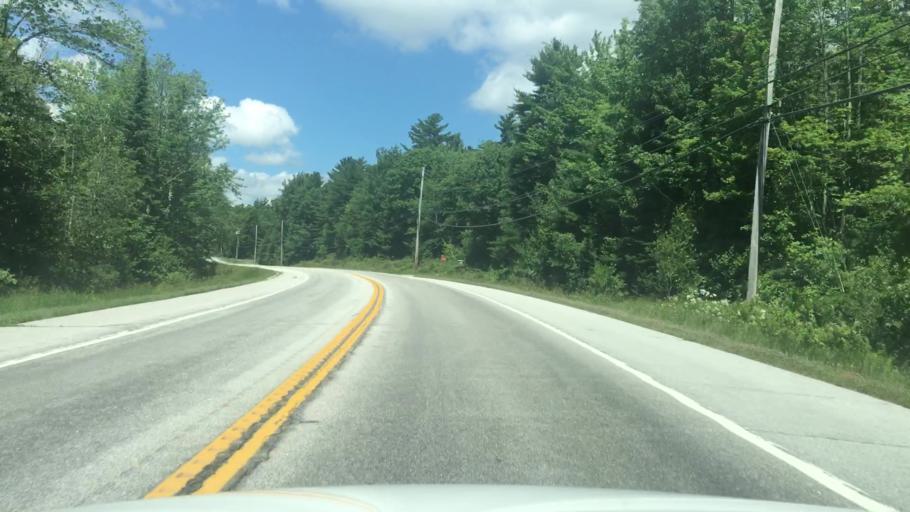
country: US
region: Maine
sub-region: Waldo County
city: Northport
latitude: 44.3558
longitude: -68.9683
